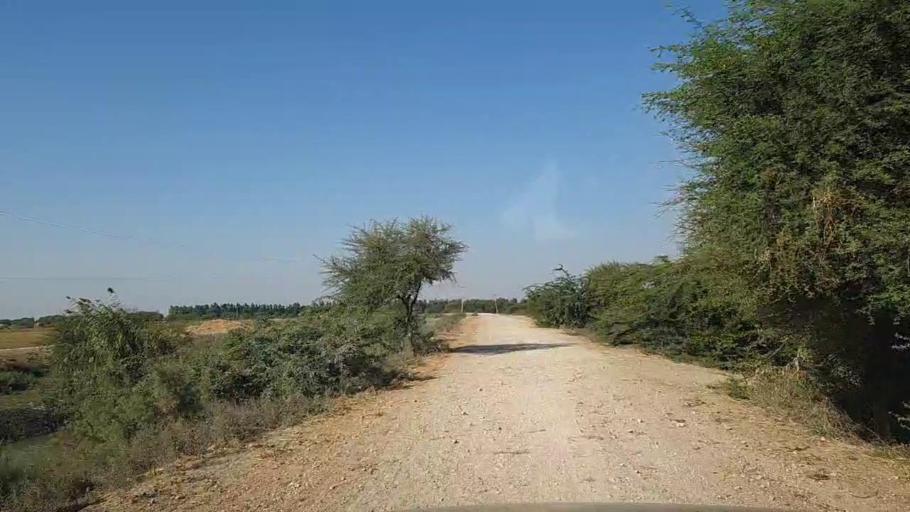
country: PK
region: Sindh
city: Mirpur Batoro
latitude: 24.7324
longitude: 68.3455
